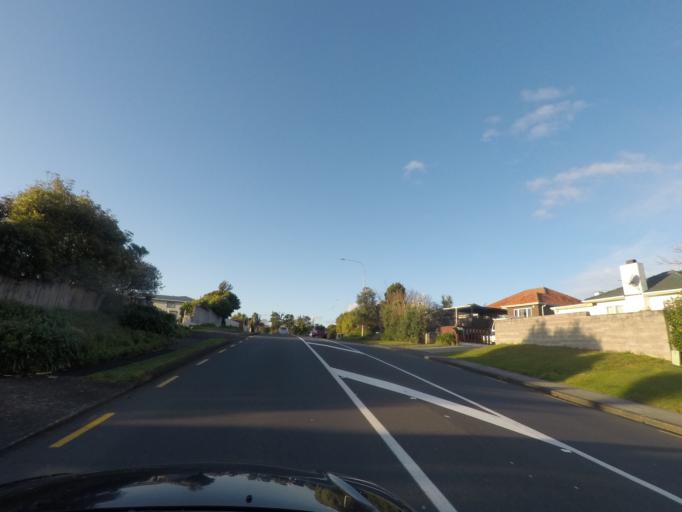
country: NZ
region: Auckland
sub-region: Auckland
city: Rosebank
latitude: -36.8692
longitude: 174.6400
